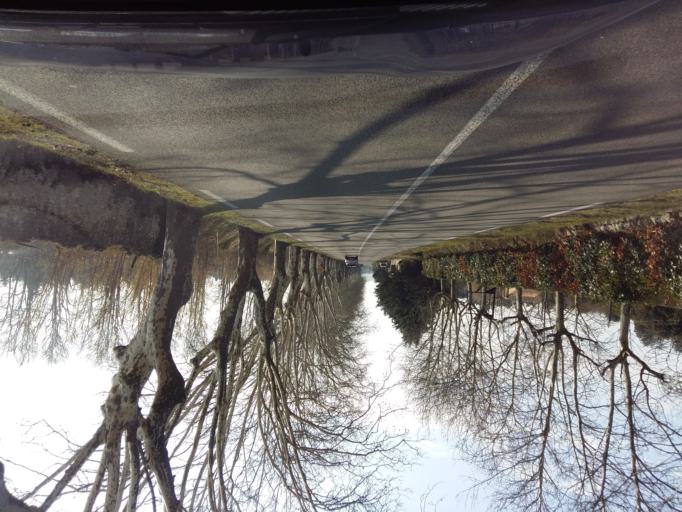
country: FR
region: Provence-Alpes-Cote d'Azur
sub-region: Departement des Bouches-du-Rhone
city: Orgon
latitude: 43.8002
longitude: 5.0061
